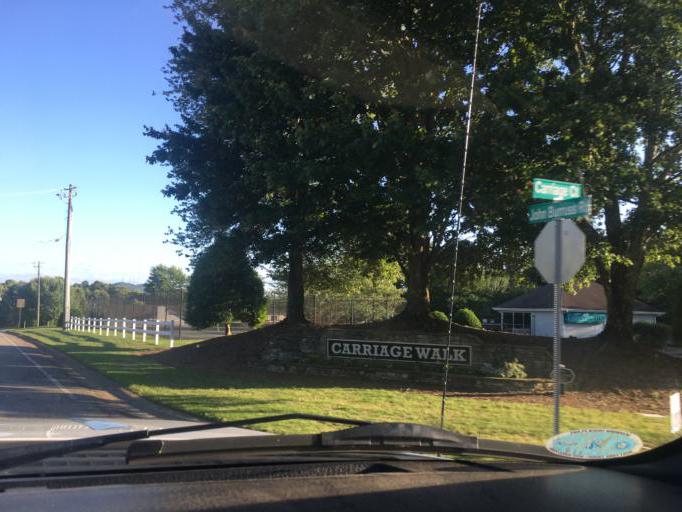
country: US
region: Georgia
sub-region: Forsyth County
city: Cumming
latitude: 34.2911
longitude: -84.1546
